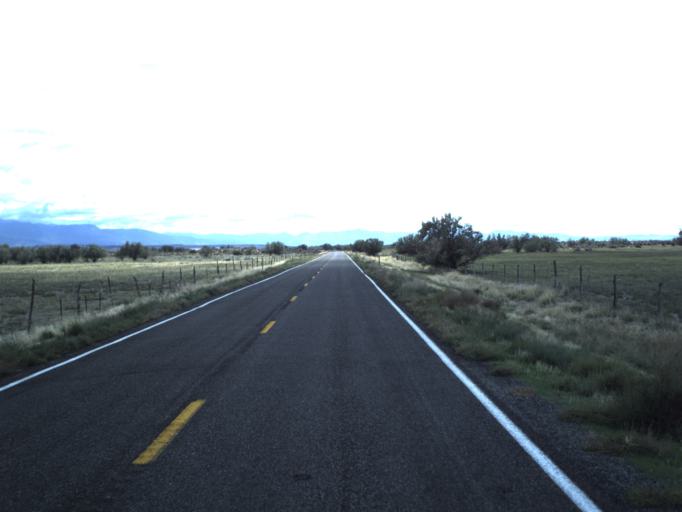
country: US
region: Utah
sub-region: Millard County
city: Fillmore
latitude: 39.1060
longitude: -112.4099
